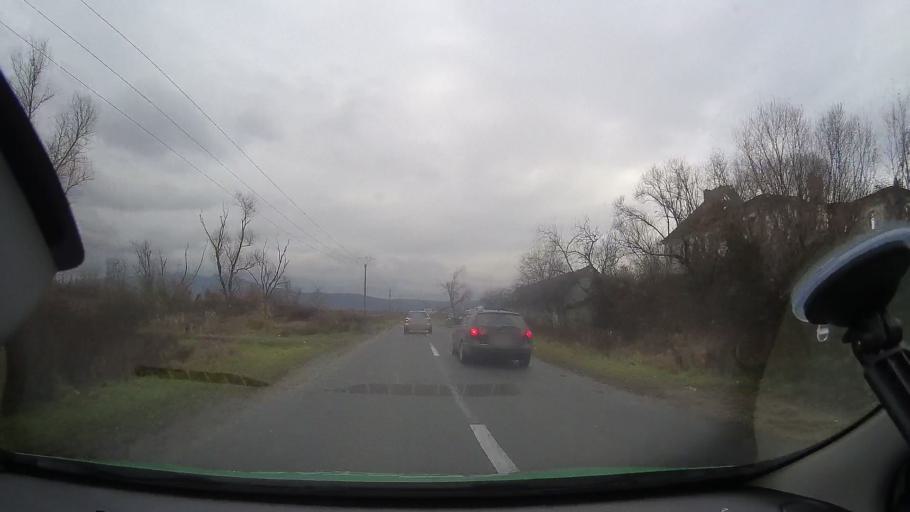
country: RO
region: Arad
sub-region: Comuna Sebis
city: Sebis
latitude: 46.3426
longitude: 22.1284
